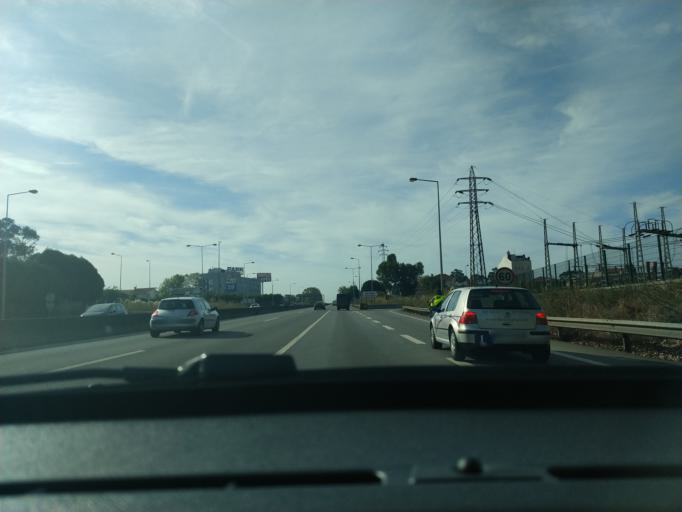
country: PT
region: Porto
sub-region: Vila Nova de Gaia
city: Canidelo
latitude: 41.1290
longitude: -8.6358
